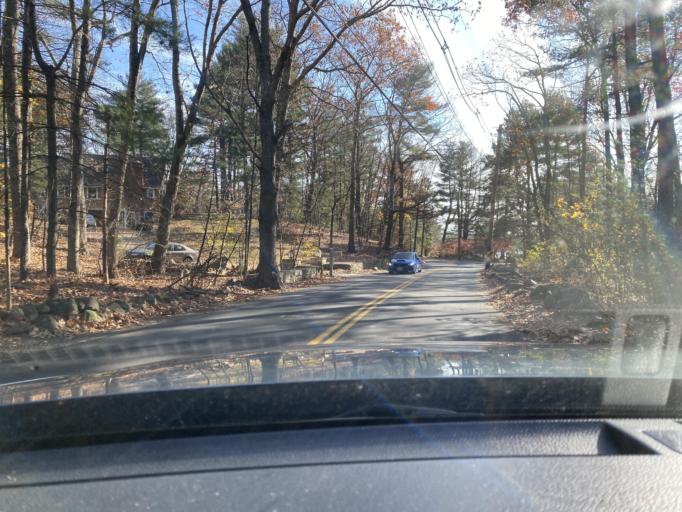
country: US
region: Massachusetts
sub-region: Norfolk County
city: Westwood
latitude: 42.1863
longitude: -71.2382
